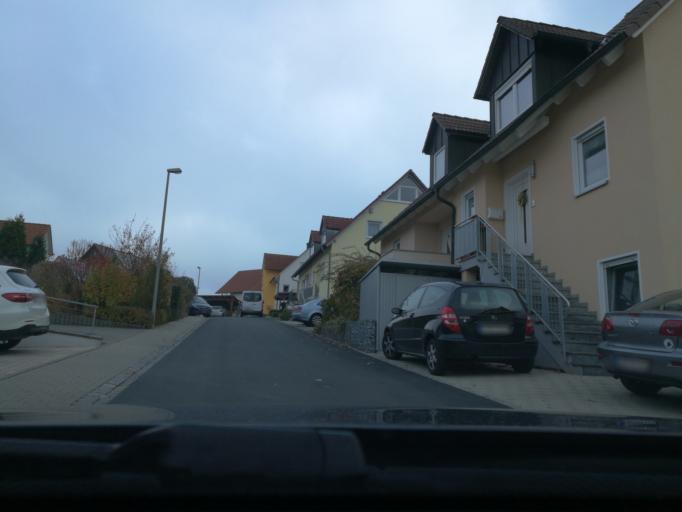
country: DE
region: Bavaria
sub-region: Regierungsbezirk Mittelfranken
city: Weisendorf
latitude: 49.5739
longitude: 10.8284
